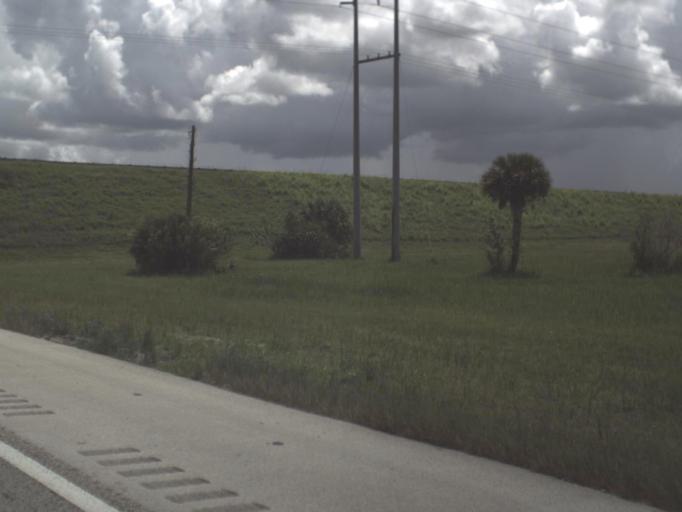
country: US
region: Florida
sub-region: Collier County
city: Immokalee
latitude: 26.1545
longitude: -81.3461
